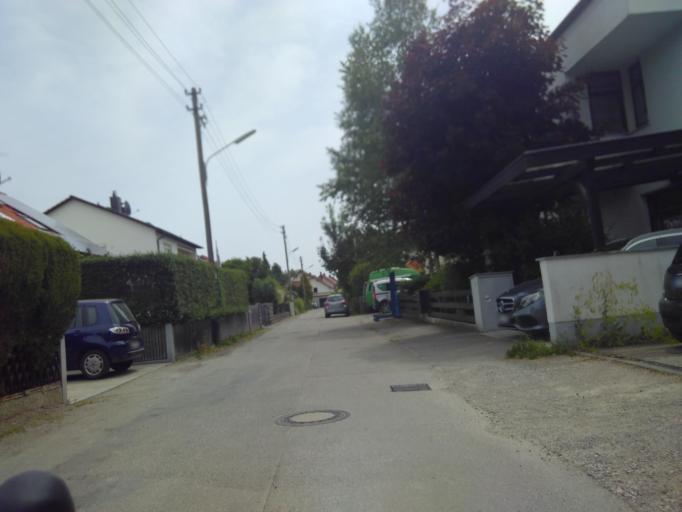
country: DE
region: Bavaria
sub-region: Upper Bavaria
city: Eichenau
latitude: 48.1614
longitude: 11.3142
